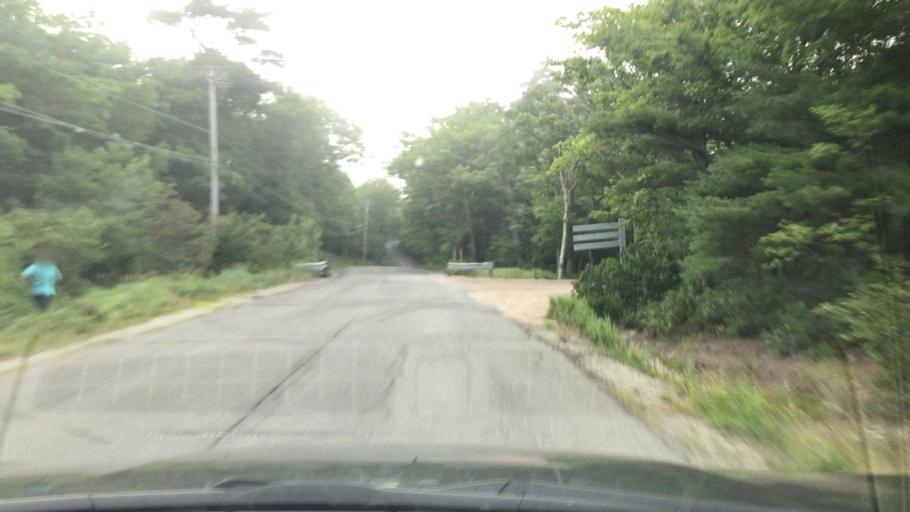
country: US
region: Maine
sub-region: Hancock County
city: Bar Harbor
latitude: 44.3554
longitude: -68.1848
